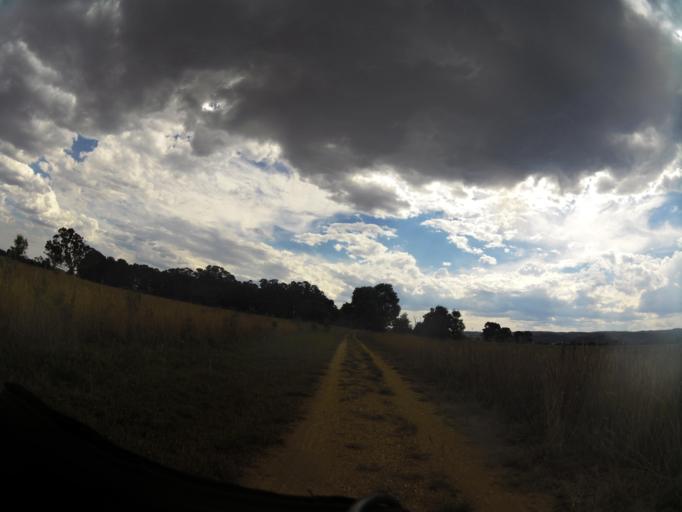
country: AU
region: Victoria
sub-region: Wellington
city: Heyfield
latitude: -38.0162
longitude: 146.6889
